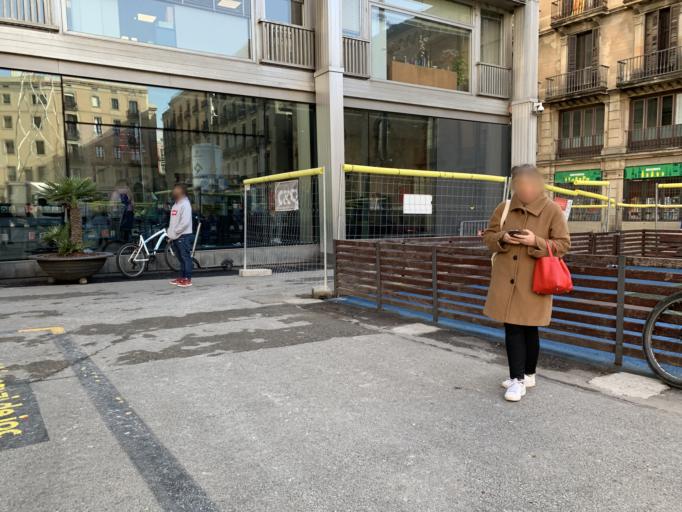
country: ES
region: Catalonia
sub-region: Provincia de Barcelona
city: Ciutat Vella
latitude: 41.3820
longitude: 2.1773
